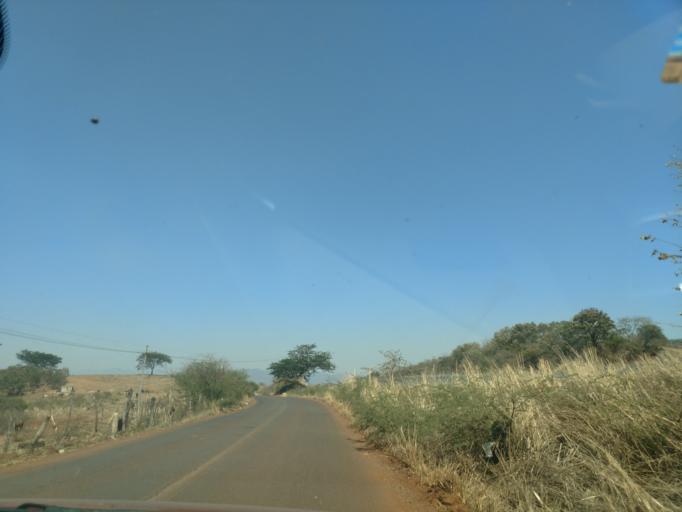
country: MX
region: Nayarit
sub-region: Tepic
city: La Corregidora
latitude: 21.4893
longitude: -104.6803
